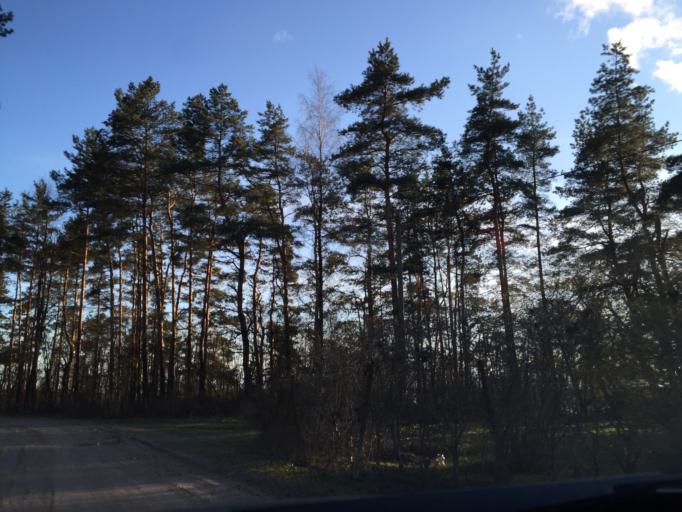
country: LV
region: Kekava
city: Kekava
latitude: 56.8549
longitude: 24.2233
